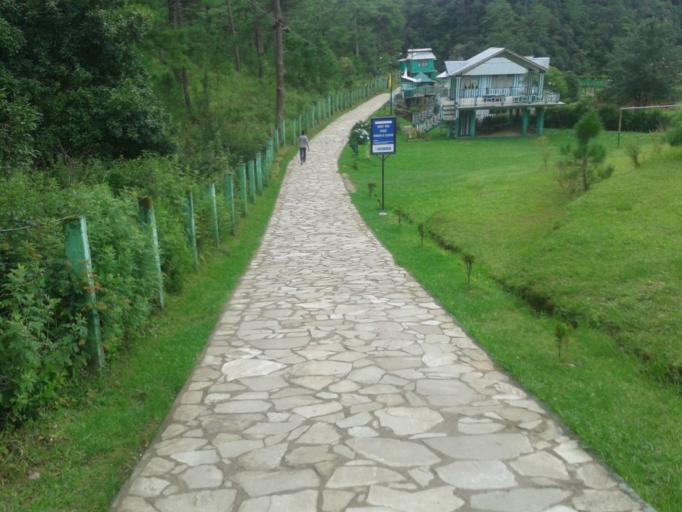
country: IN
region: Meghalaya
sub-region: East Khasi Hills
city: Shillong
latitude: 25.5400
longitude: 91.8216
